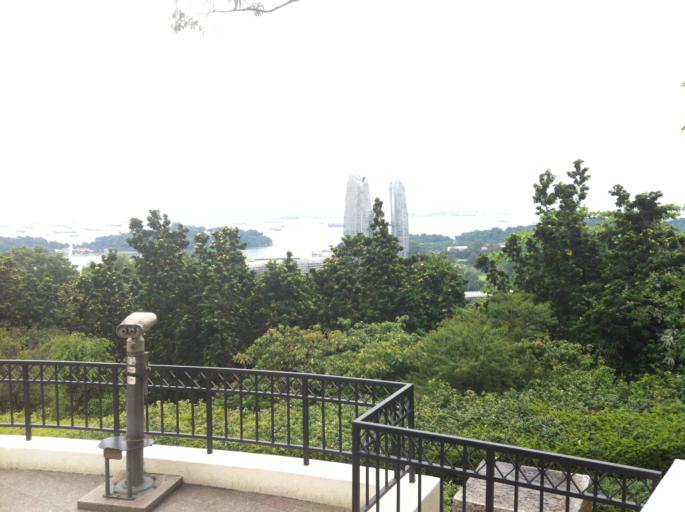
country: SG
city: Singapore
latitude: 1.2735
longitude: 103.8175
